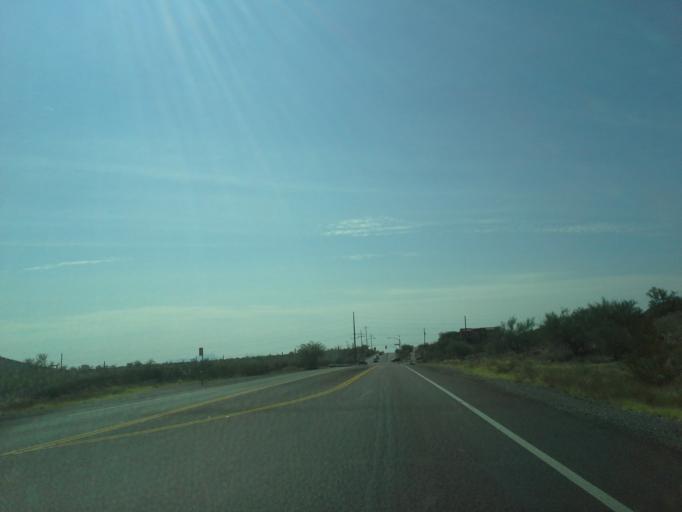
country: US
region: Arizona
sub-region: Pima County
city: South Tucson
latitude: 32.2276
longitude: -111.0203
